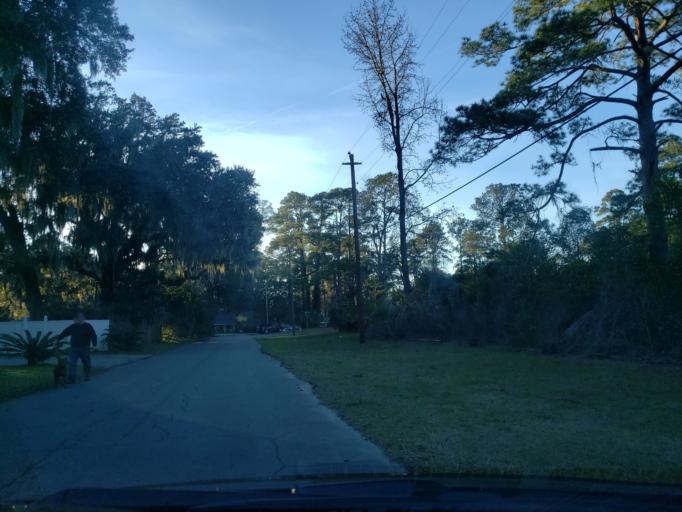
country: US
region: Georgia
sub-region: Chatham County
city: Isle of Hope
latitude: 31.9919
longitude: -81.1103
